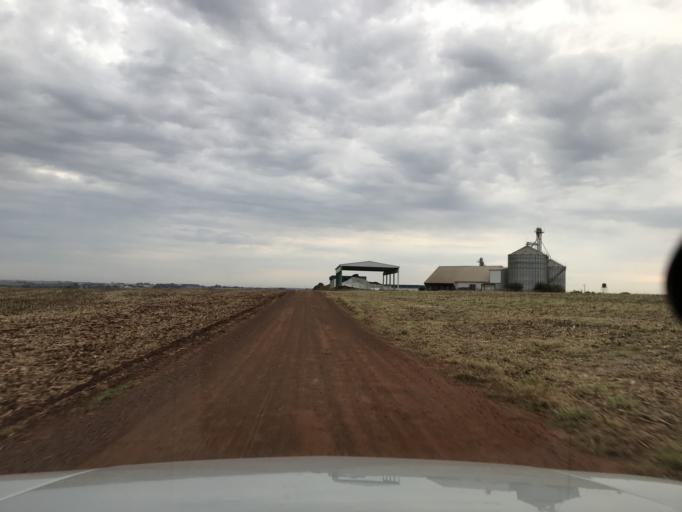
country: BR
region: Parana
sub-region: Palotina
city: Palotina
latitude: -24.2272
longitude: -53.8412
